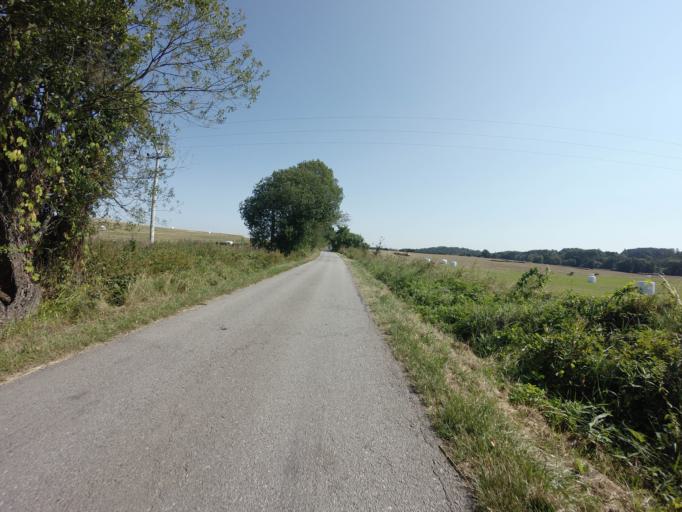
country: CZ
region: Jihocesky
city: Kamenny Ujezd
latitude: 48.8795
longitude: 14.3968
